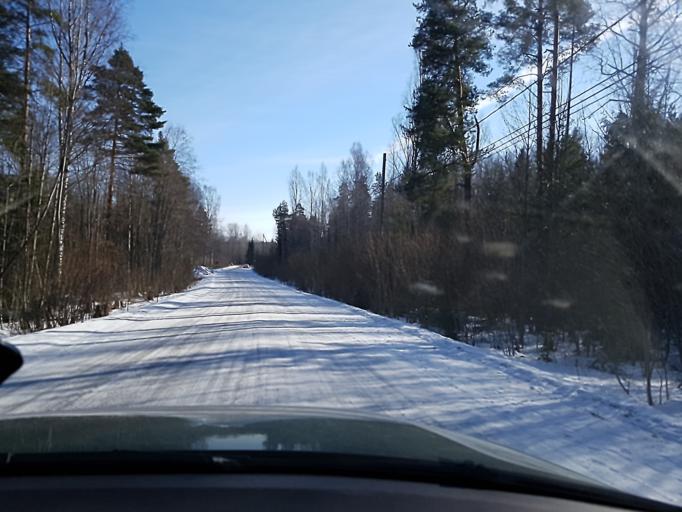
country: FI
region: Uusimaa
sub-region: Helsinki
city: Lohja
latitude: 60.1748
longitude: 23.9677
